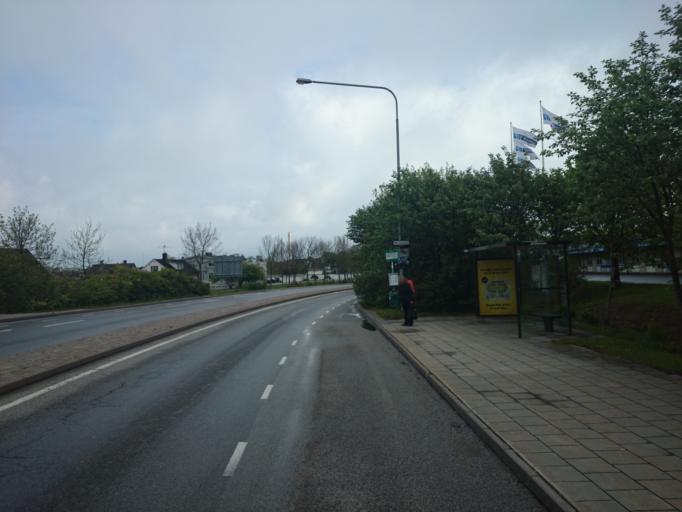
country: SE
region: Skane
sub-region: Malmo
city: Bunkeflostrand
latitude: 55.5763
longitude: 12.9261
